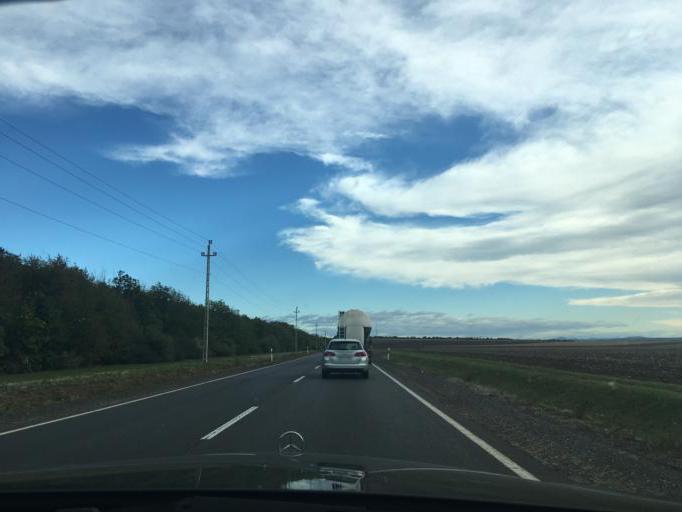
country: HU
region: Borsod-Abauj-Zemplen
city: Arnot
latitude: 48.1355
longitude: 20.8808
